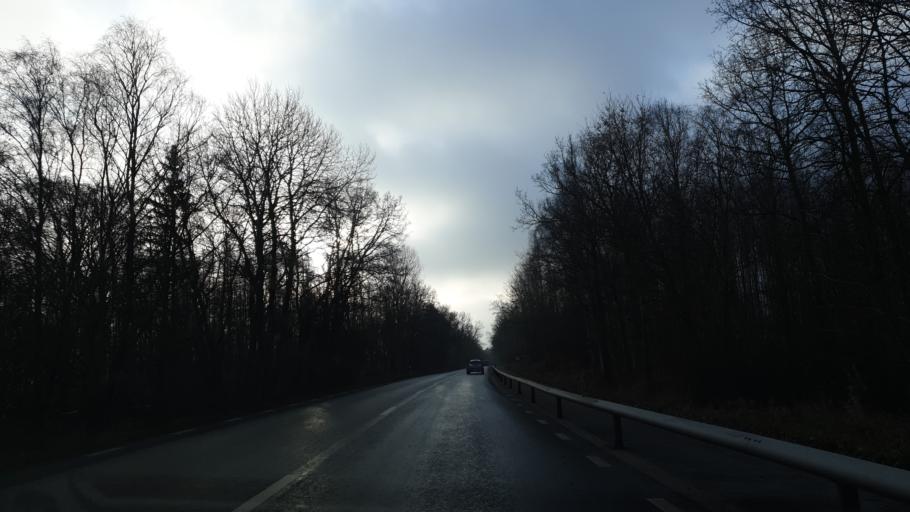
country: SE
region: Blekinge
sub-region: Karlshamns Kommun
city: Morrum
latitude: 56.1327
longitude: 14.6726
